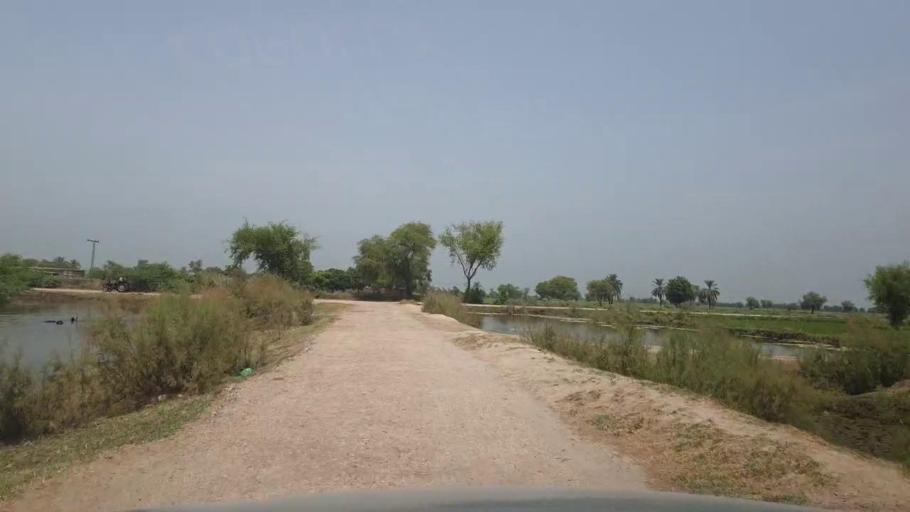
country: PK
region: Sindh
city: Garhi Yasin
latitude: 27.9216
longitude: 68.3754
